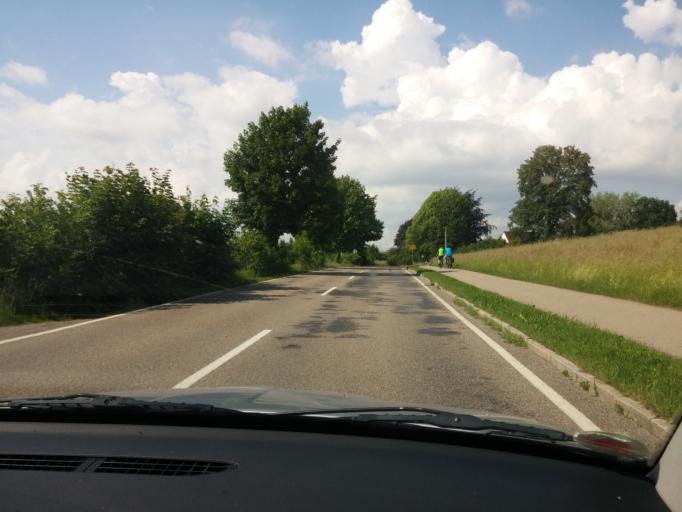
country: DE
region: Bavaria
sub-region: Swabia
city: Buxheim
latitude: 47.9915
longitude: 10.1368
